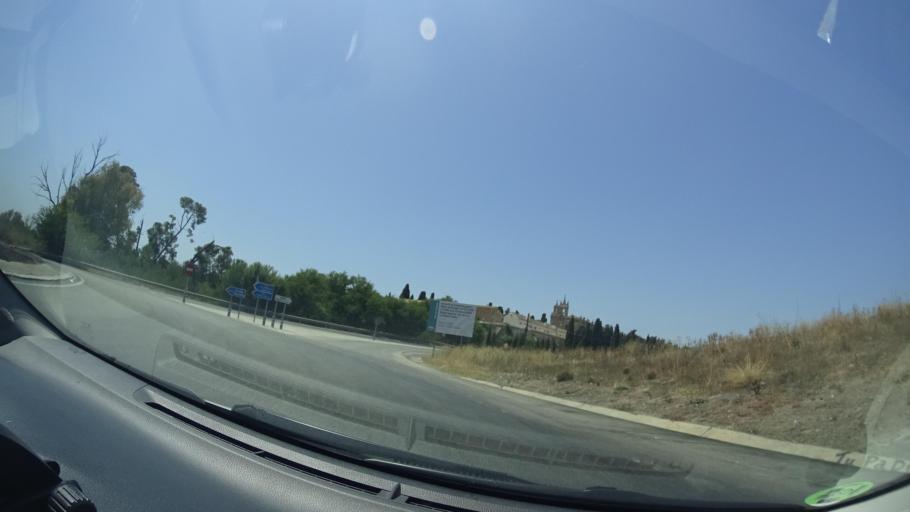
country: ES
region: Andalusia
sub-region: Provincia de Cadiz
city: Jerez de la Frontera
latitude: 36.6539
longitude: -6.0896
